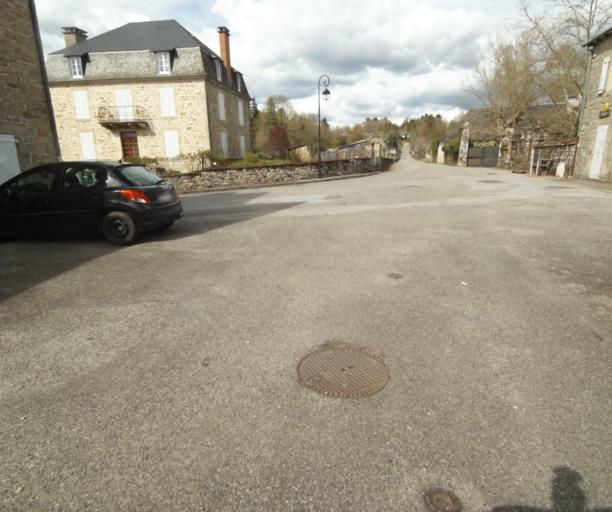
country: FR
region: Limousin
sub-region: Departement de la Correze
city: Argentat
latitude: 45.1855
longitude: 1.9516
